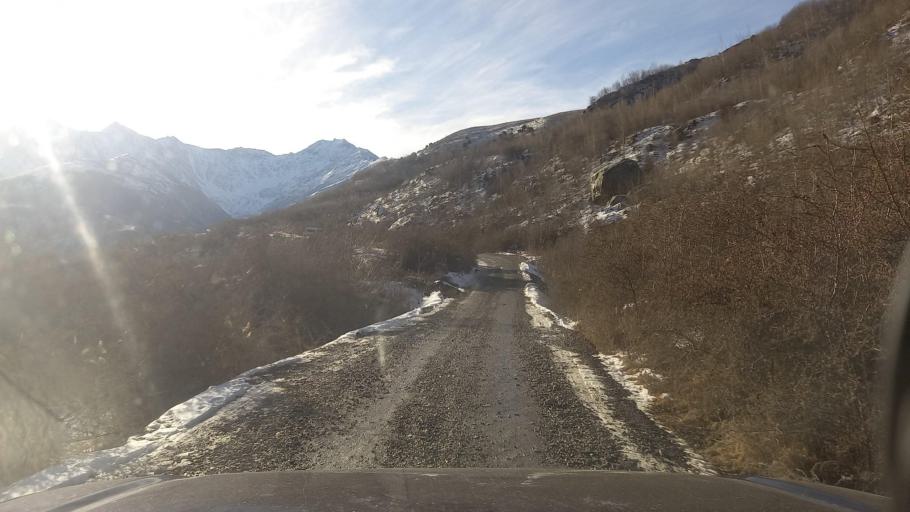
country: RU
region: Ingushetiya
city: Dzhayrakh
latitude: 42.8613
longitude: 44.5199
